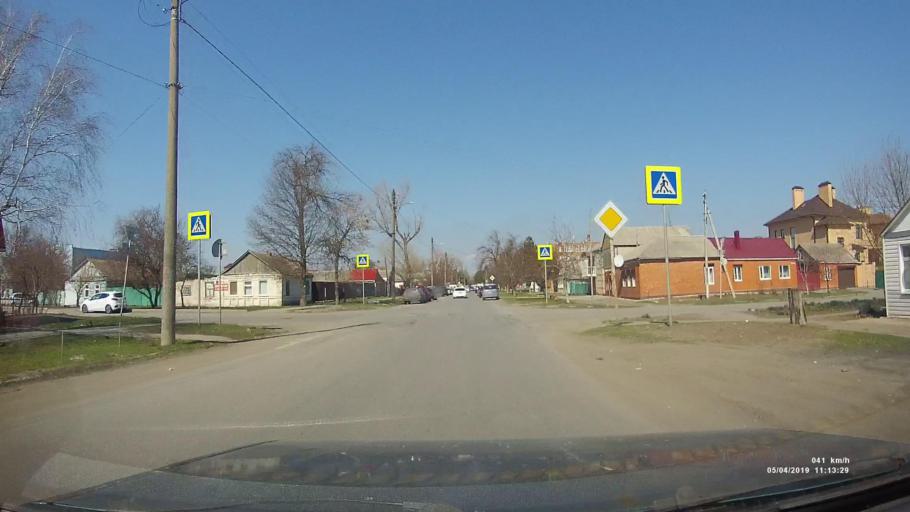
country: RU
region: Rostov
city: Azov
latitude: 47.1023
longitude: 39.4311
